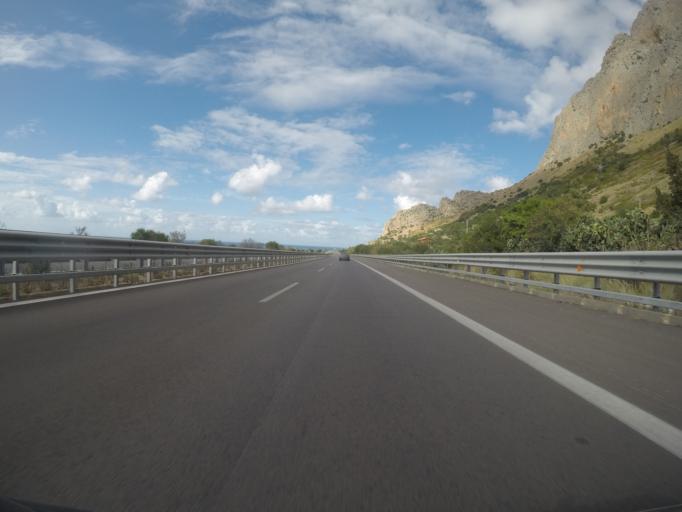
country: IT
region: Sicily
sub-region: Palermo
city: Cinisi
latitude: 38.1624
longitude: 13.1137
